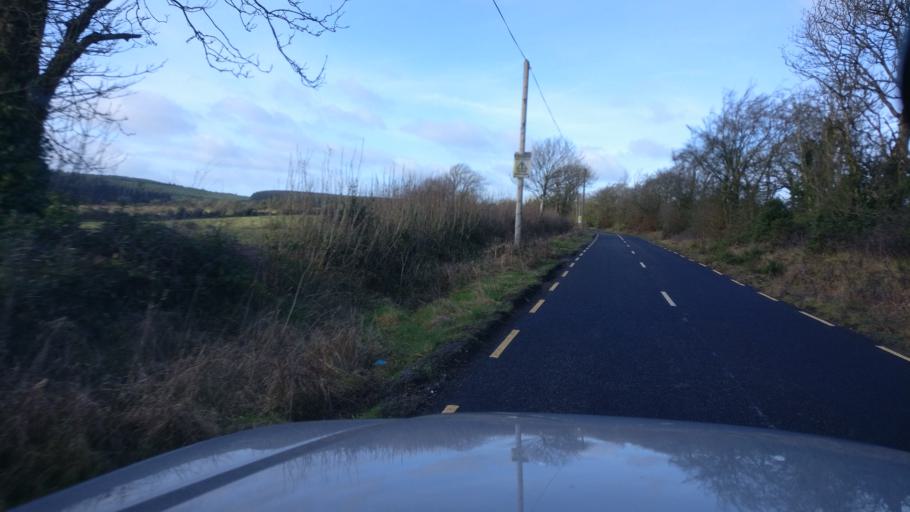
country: IE
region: Leinster
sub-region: Kilkenny
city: Castlecomer
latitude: 52.9010
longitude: -7.1762
